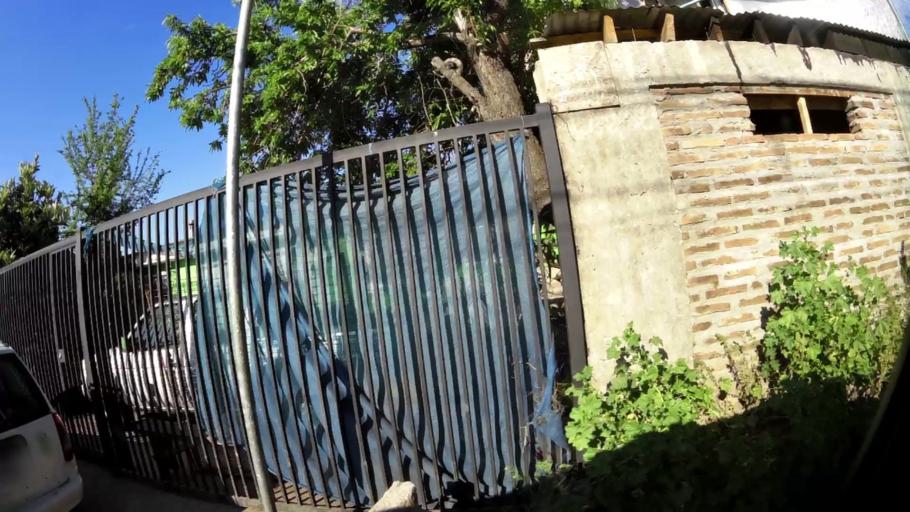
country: CL
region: Santiago Metropolitan
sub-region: Provincia de Santiago
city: Lo Prado
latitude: -33.4877
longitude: -70.7604
